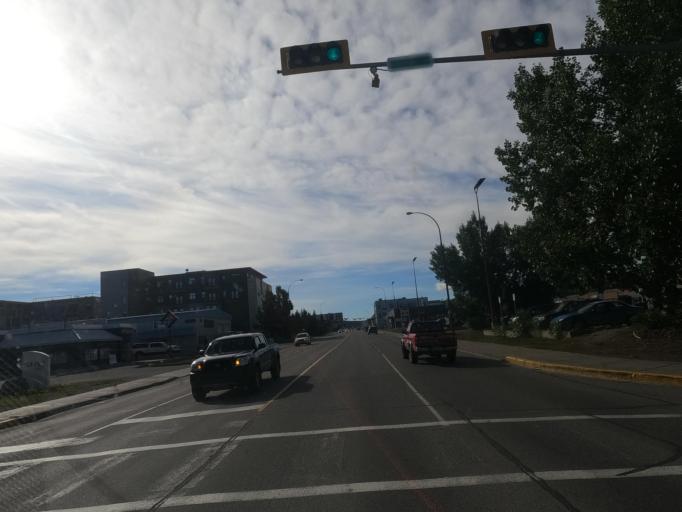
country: CA
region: Yukon
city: Whitehorse
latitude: 60.7264
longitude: -135.0576
